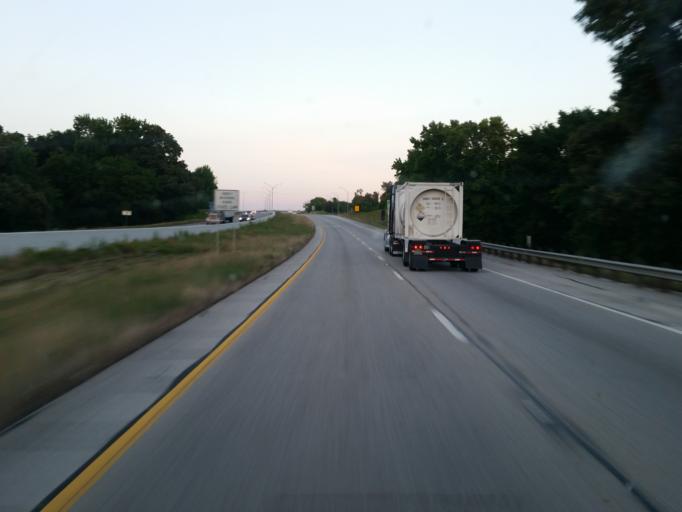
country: US
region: Texas
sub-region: Smith County
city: Hideaway
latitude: 32.4705
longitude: -95.4611
